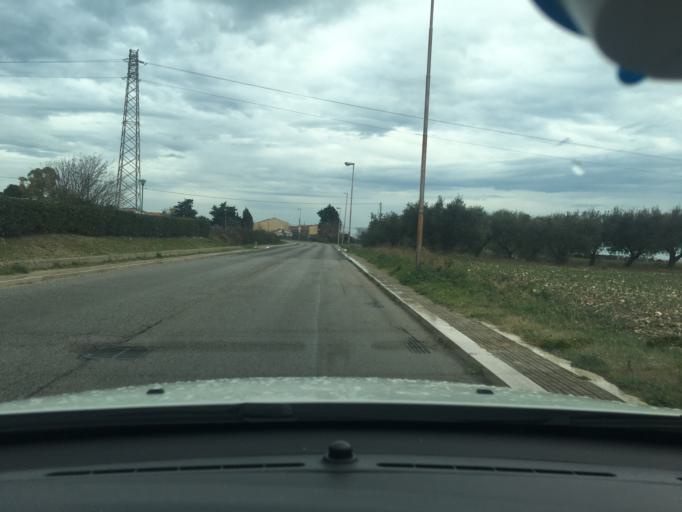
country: IT
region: Molise
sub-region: Provincia di Campobasso
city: Termoli
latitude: 41.9749
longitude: 14.9951
